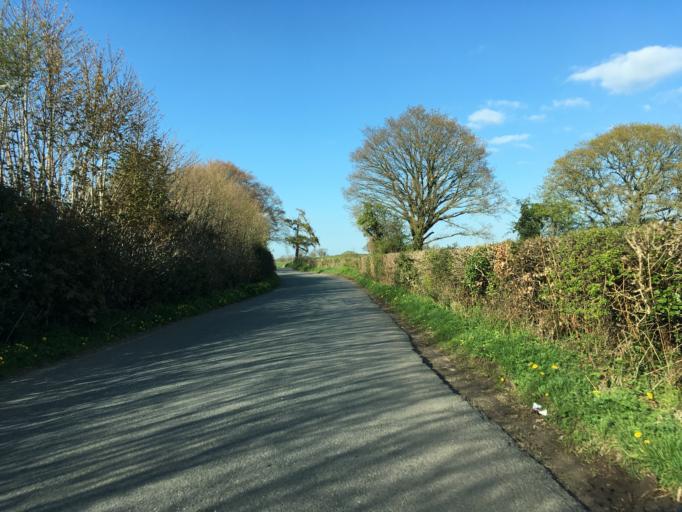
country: GB
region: Wales
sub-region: Torfaen County Borough
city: New Inn
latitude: 51.6978
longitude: -2.9987
